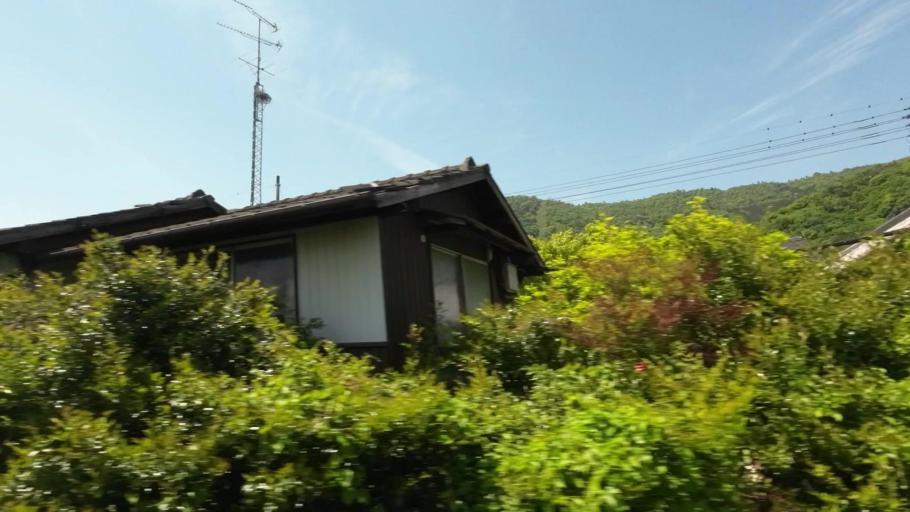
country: JP
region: Kagawa
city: Marugame
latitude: 34.1991
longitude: 133.8103
